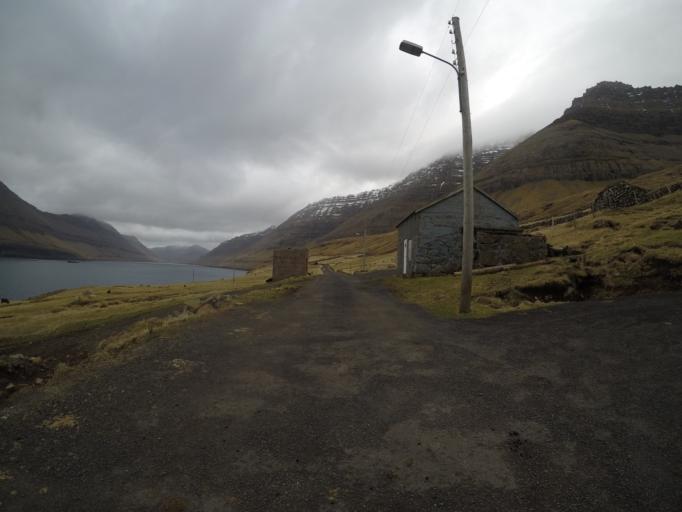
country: FO
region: Nordoyar
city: Klaksvik
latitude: 62.3508
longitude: -6.5825
